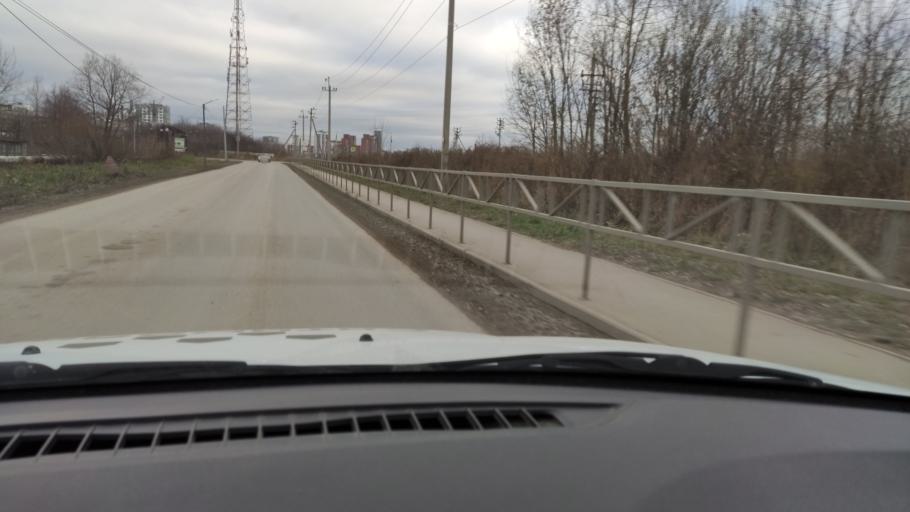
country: RU
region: Perm
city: Kondratovo
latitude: 57.9826
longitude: 56.1153
